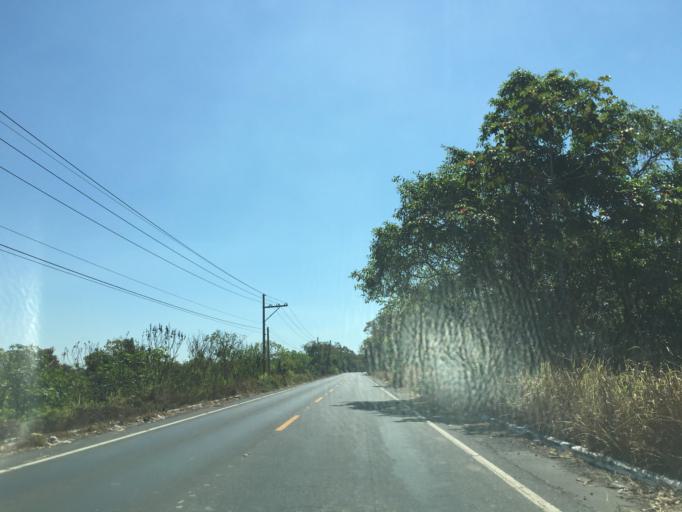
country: GT
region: Escuintla
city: Puerto San Jose
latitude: 13.9817
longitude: -90.8906
